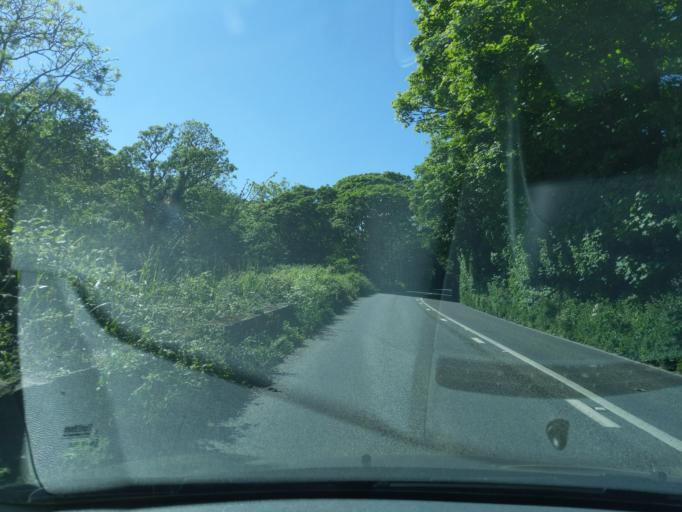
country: GB
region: England
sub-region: Cornwall
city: Porthleven
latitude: 50.1041
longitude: -5.3285
